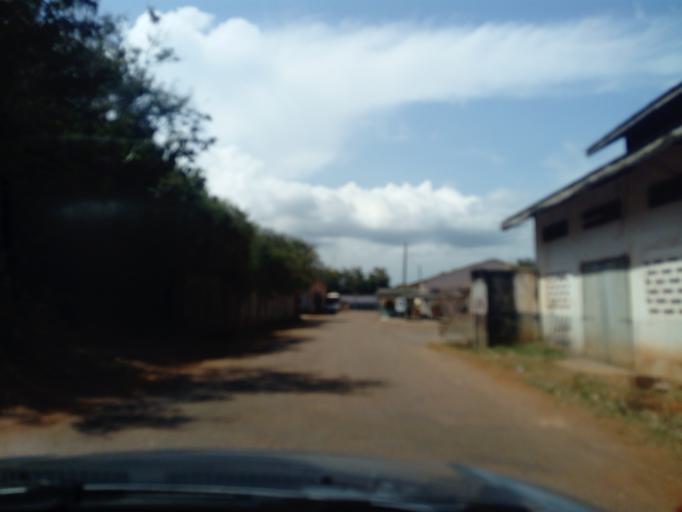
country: GH
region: Central
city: Cape Coast
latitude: 5.1062
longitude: -1.2803
